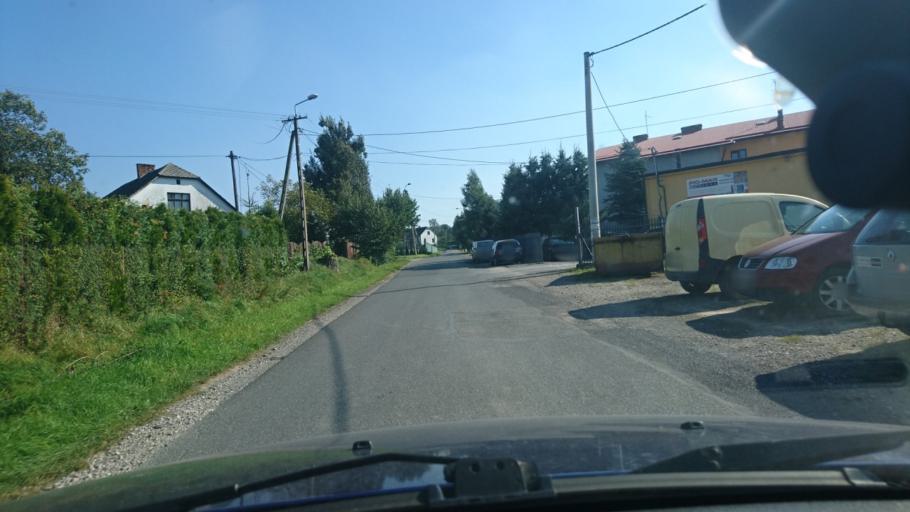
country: PL
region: Silesian Voivodeship
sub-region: Bielsko-Biala
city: Bielsko-Biala
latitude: 49.8504
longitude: 19.0739
